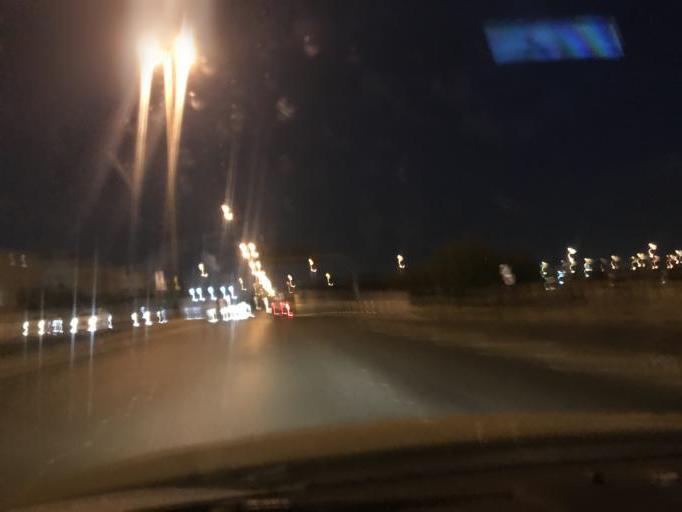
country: SA
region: Ar Riyad
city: Riyadh
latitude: 24.6673
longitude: 46.7902
